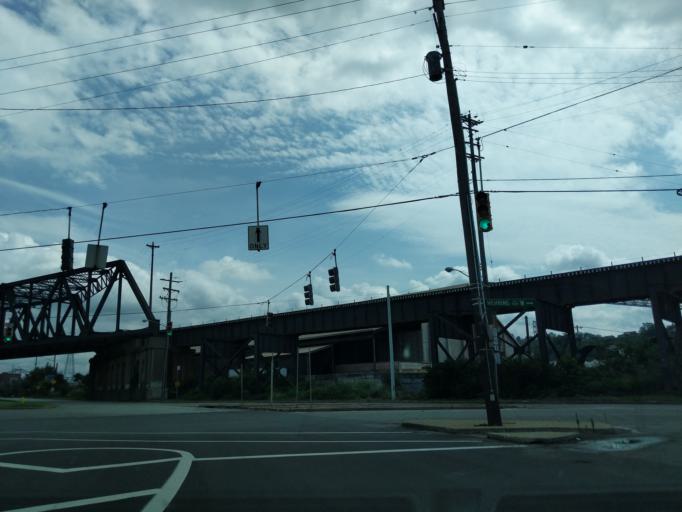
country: US
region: Kentucky
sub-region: Kenton County
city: Ludlow
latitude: 39.0984
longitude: -84.5334
